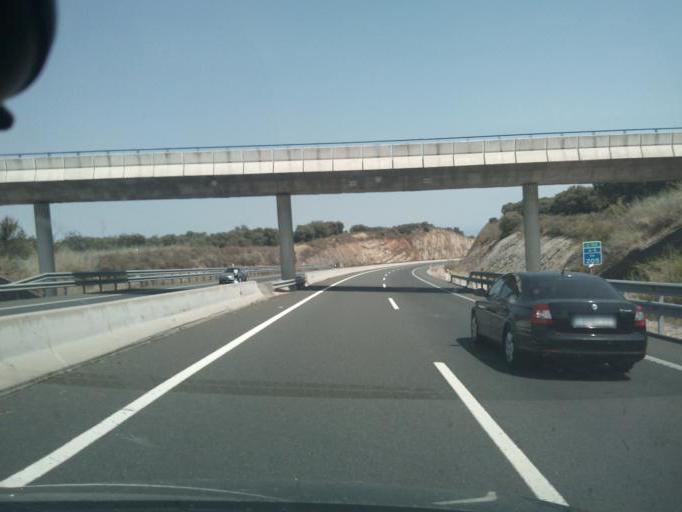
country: ES
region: Extremadura
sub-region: Provincia de Caceres
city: Casas de Miravete
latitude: 39.7731
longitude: -5.7382
